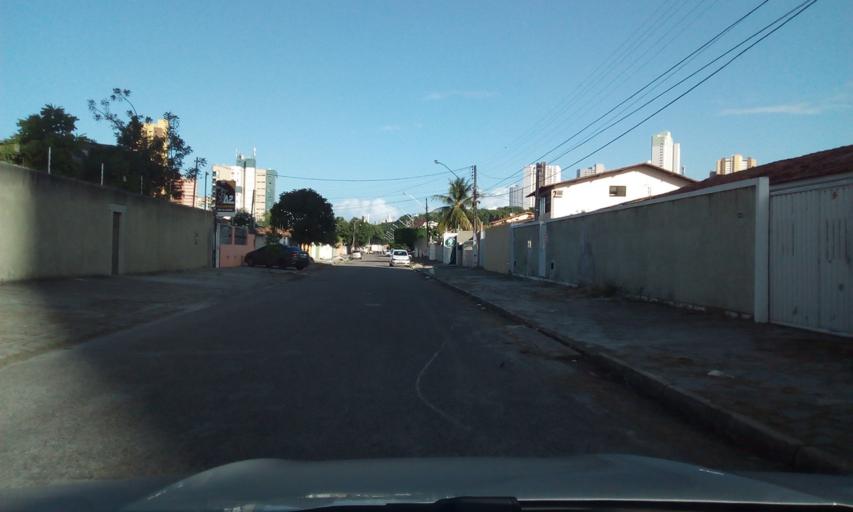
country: BR
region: Paraiba
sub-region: Joao Pessoa
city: Joao Pessoa
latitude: -7.1069
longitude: -34.8387
